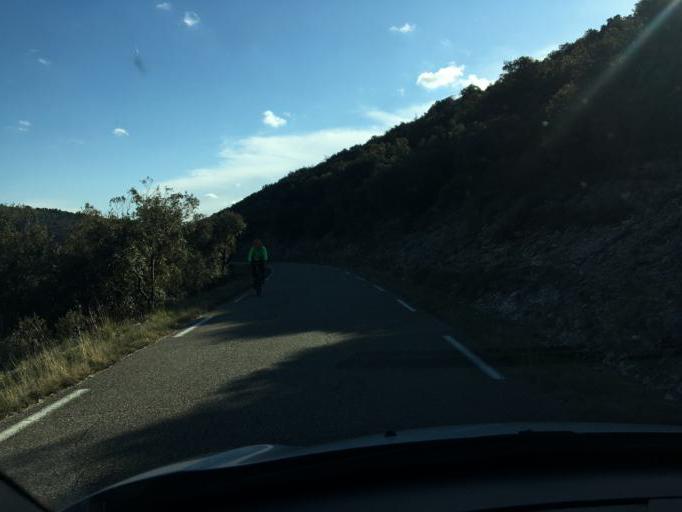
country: FR
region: Provence-Alpes-Cote d'Azur
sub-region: Departement du Vaucluse
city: Villes-sur-Auzon
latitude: 44.0387
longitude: 5.2665
